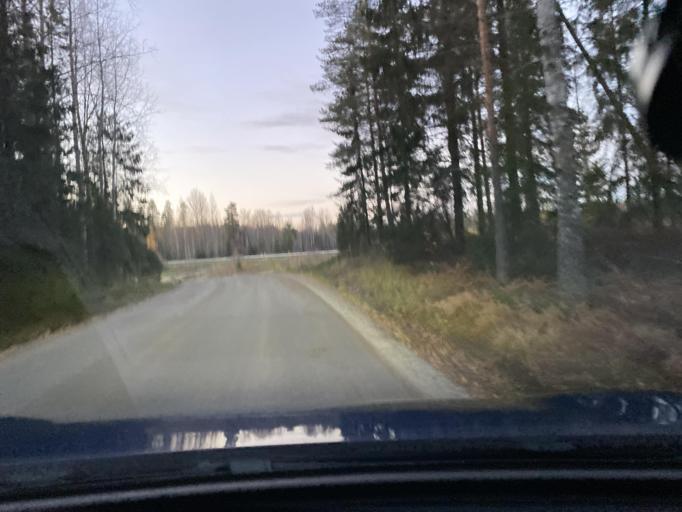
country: FI
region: Uusimaa
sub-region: Porvoo
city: Pukkila
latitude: 60.7684
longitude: 25.5237
